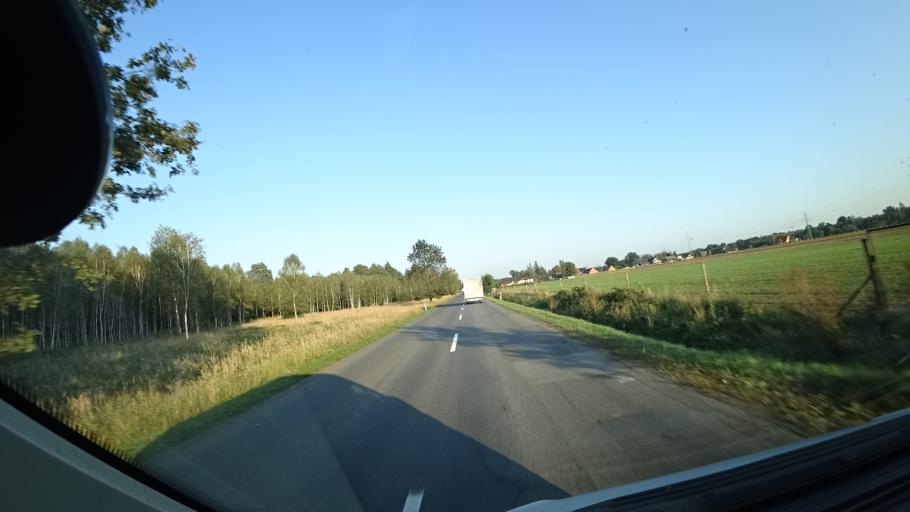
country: PL
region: Silesian Voivodeship
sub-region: Powiat gliwicki
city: Rudziniec
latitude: 50.2702
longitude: 18.4071
